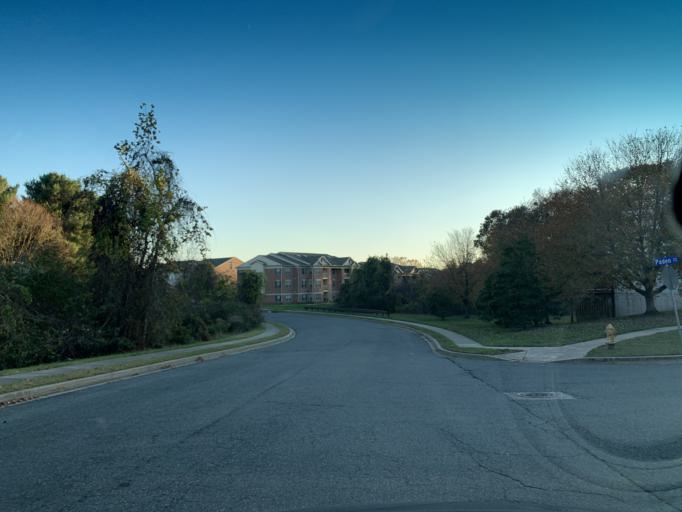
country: US
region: Maryland
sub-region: Harford County
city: Bel Air North
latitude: 39.5655
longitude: -76.3772
